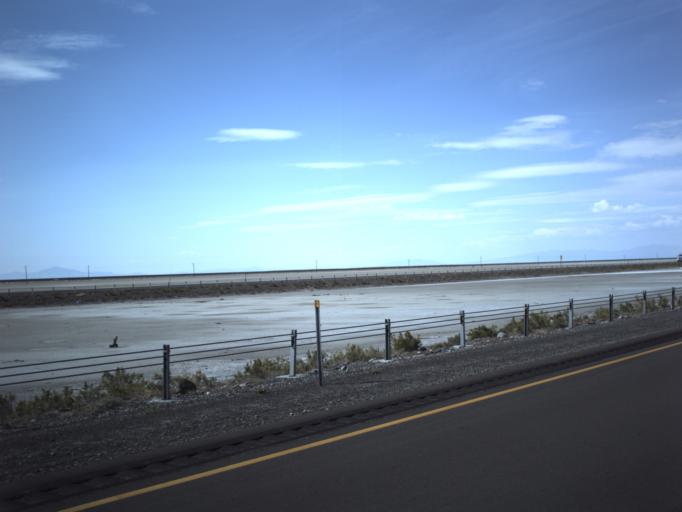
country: US
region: Utah
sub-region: Tooele County
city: Wendover
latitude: 40.7289
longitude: -113.3663
